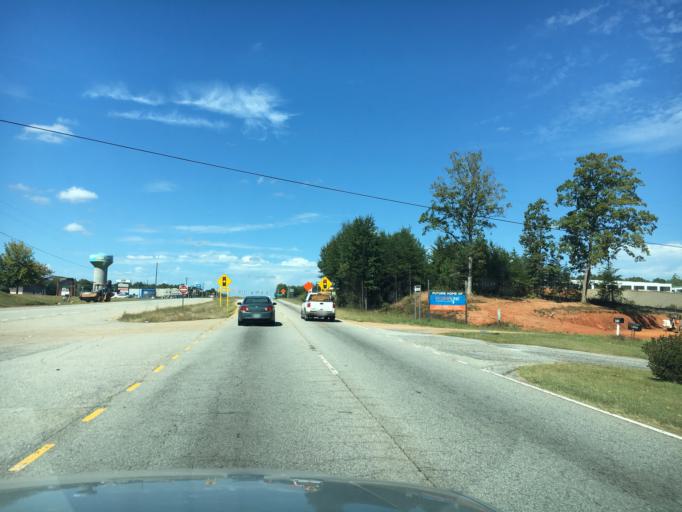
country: US
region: South Carolina
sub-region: Anderson County
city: Powdersville
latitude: 34.8104
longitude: -82.5148
